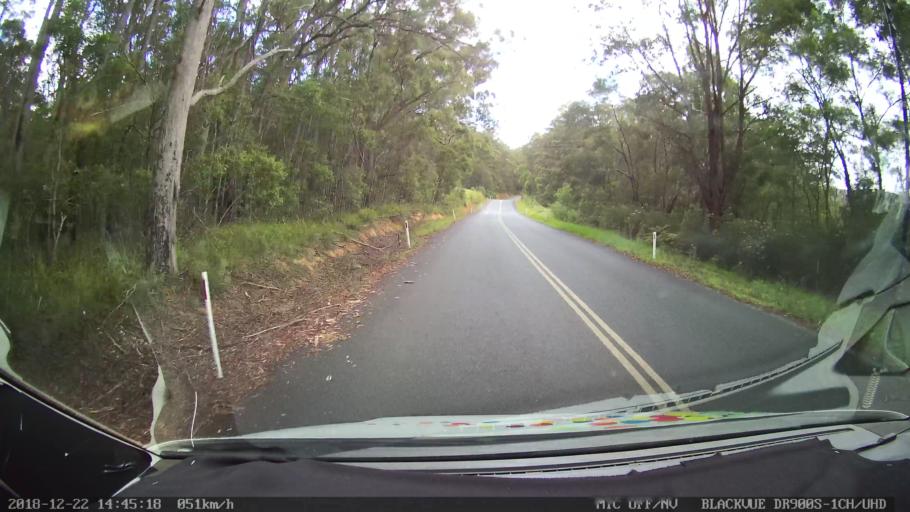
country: AU
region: New South Wales
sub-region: Bellingen
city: Dorrigo
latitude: -30.1695
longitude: 152.5702
